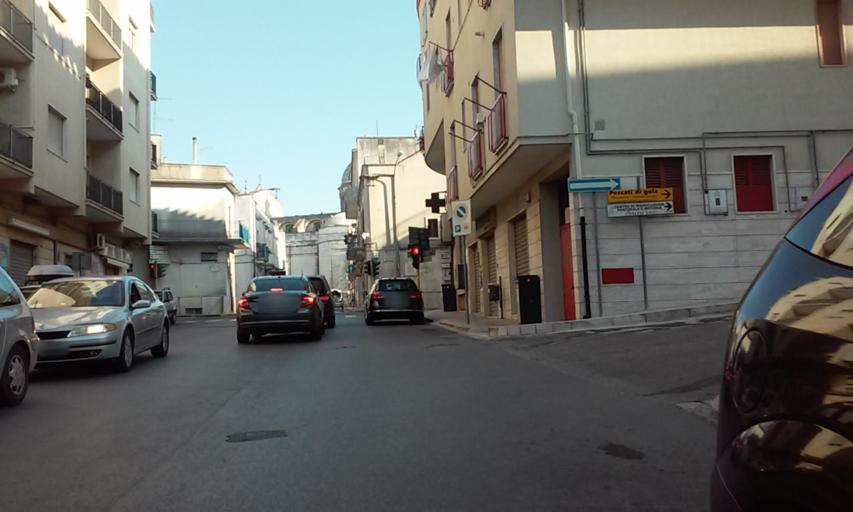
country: IT
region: Apulia
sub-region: Provincia di Brindisi
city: Ceglie Messapica
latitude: 40.6485
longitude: 17.5121
